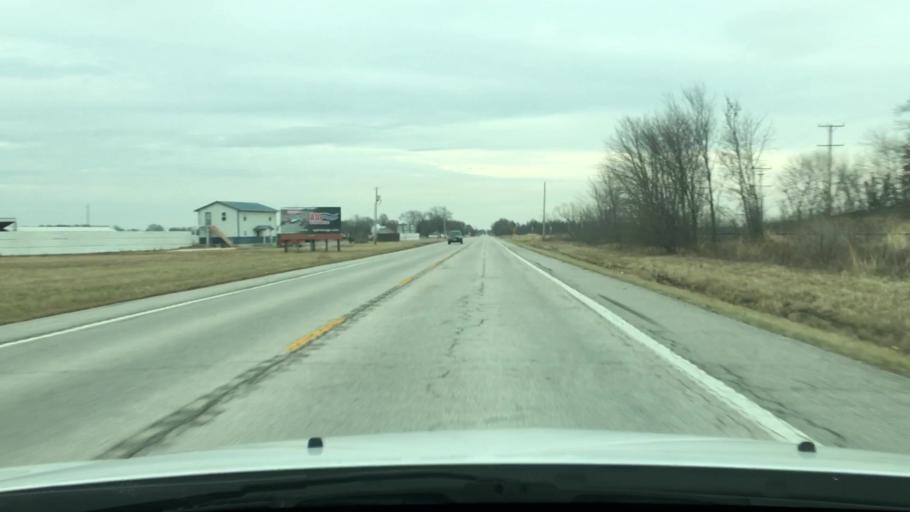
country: US
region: Missouri
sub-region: Audrain County
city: Vandalia
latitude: 39.2913
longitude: -91.5311
